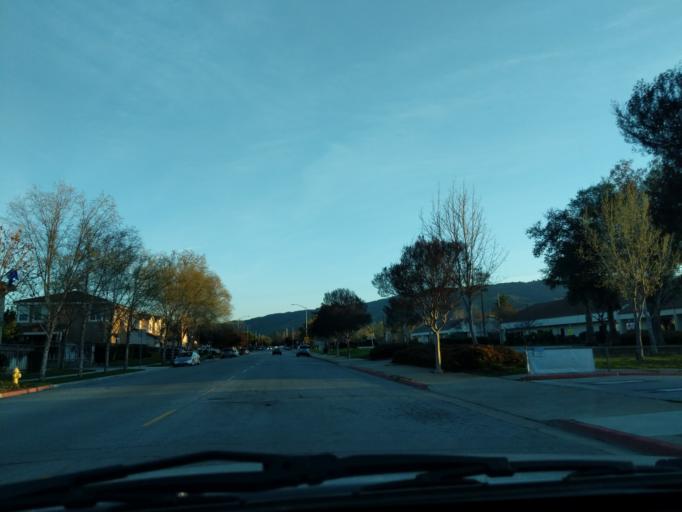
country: US
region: California
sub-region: Santa Clara County
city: Gilroy
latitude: 37.0217
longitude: -121.5916
